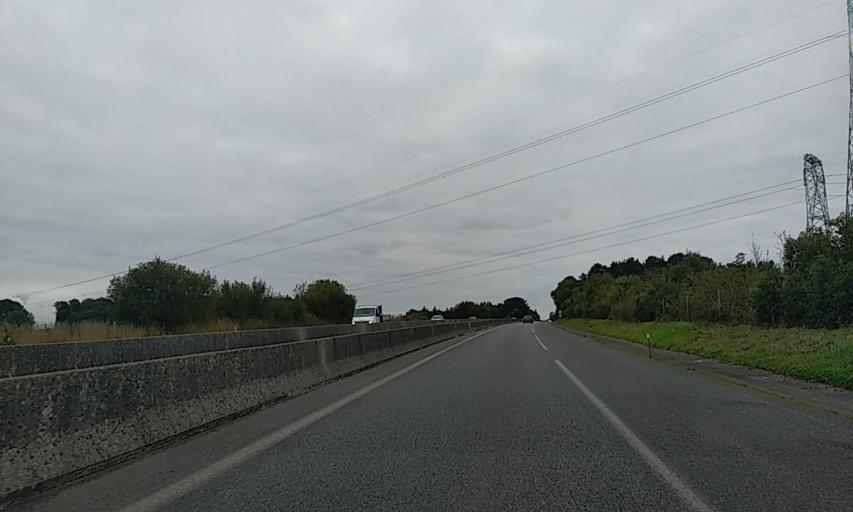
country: FR
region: Brittany
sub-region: Departement du Morbihan
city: Caudan
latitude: 47.8464
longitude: -3.3408
